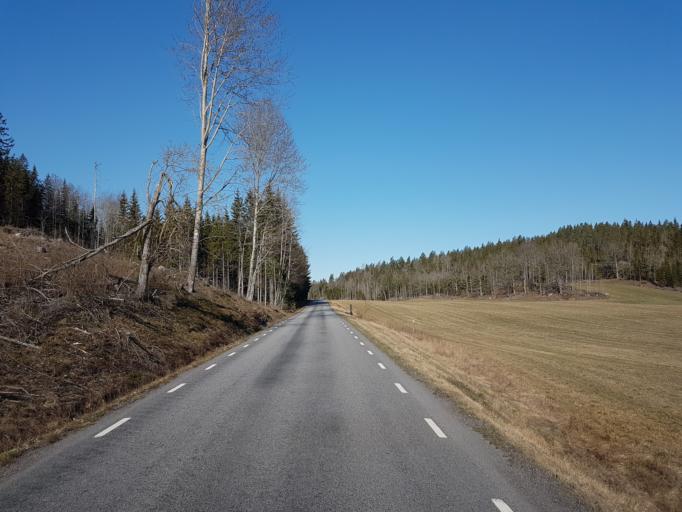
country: SE
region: OEstergoetland
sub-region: Valdemarsviks Kommun
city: Gusum
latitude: 58.1984
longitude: 16.3661
